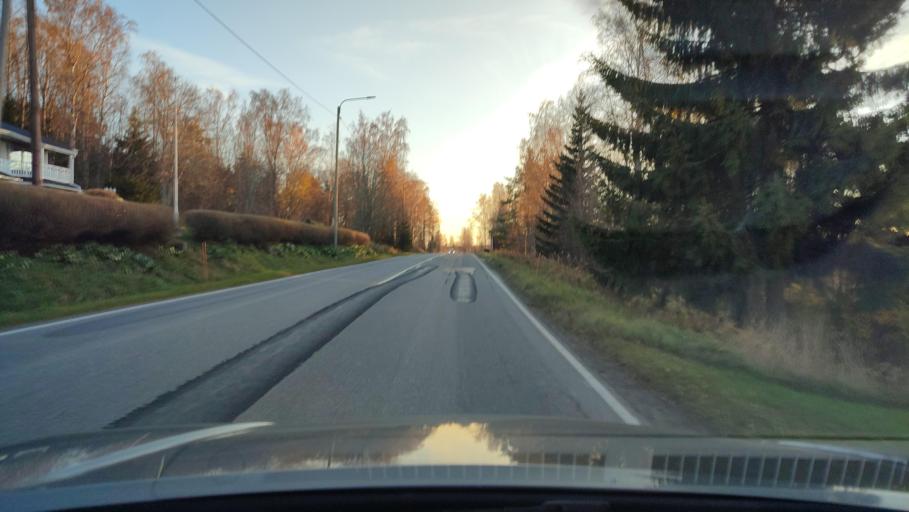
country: FI
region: Ostrobothnia
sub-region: Sydosterbotten
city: Naerpes
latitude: 62.4305
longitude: 21.3476
